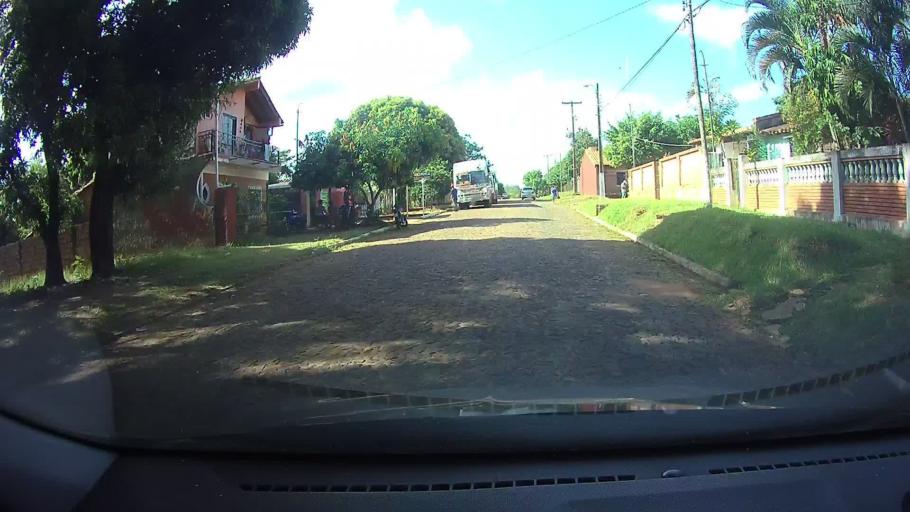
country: PY
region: Central
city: Limpio
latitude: -25.2516
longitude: -57.4707
